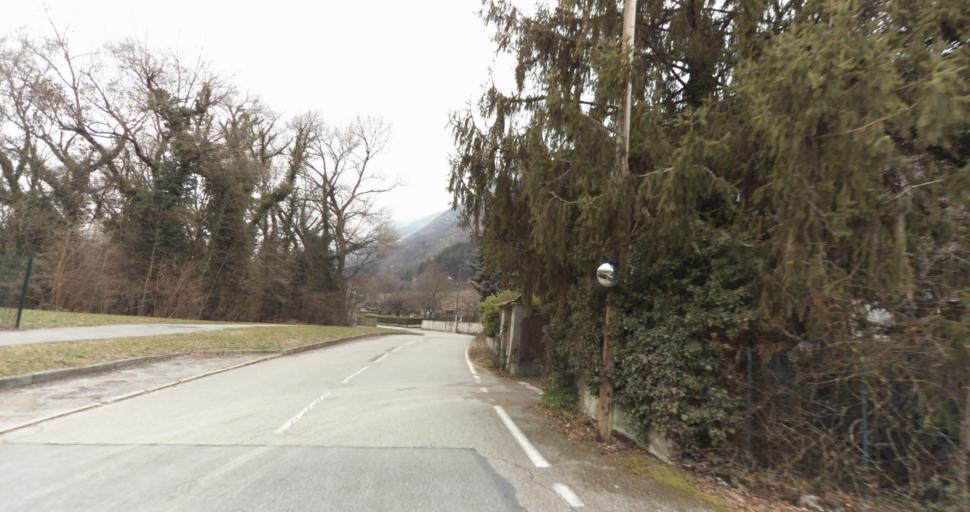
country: FR
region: Rhone-Alpes
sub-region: Departement de l'Isere
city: Vif
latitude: 45.0515
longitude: 5.6638
